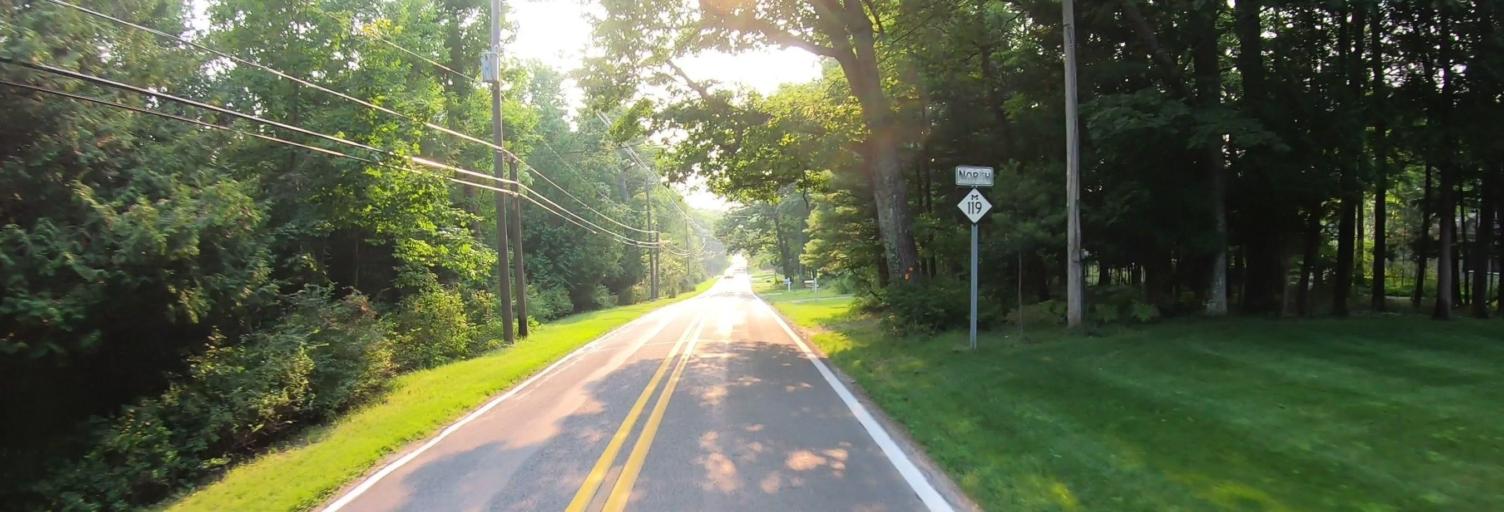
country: US
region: Michigan
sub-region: Emmet County
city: Harbor Springs
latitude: 45.4316
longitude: -85.0020
